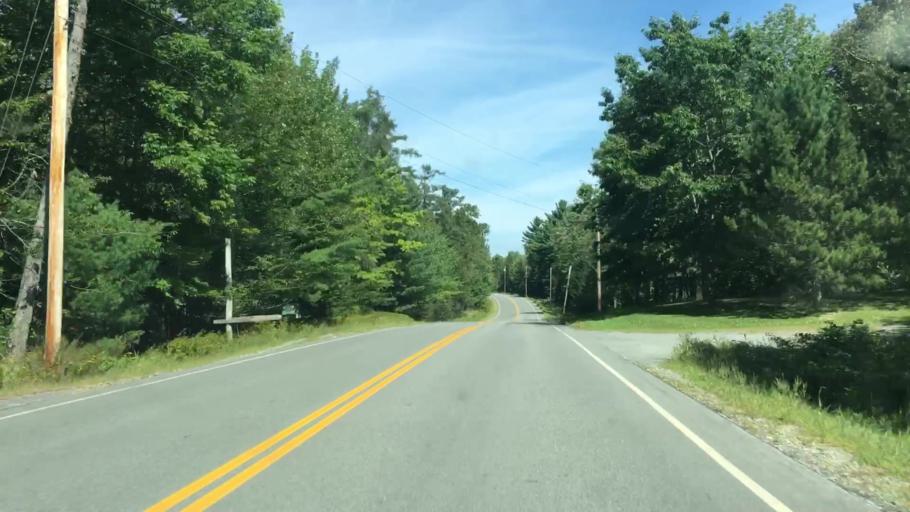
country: US
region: Maine
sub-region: Penobscot County
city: Howland
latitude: 45.2043
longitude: -68.8102
